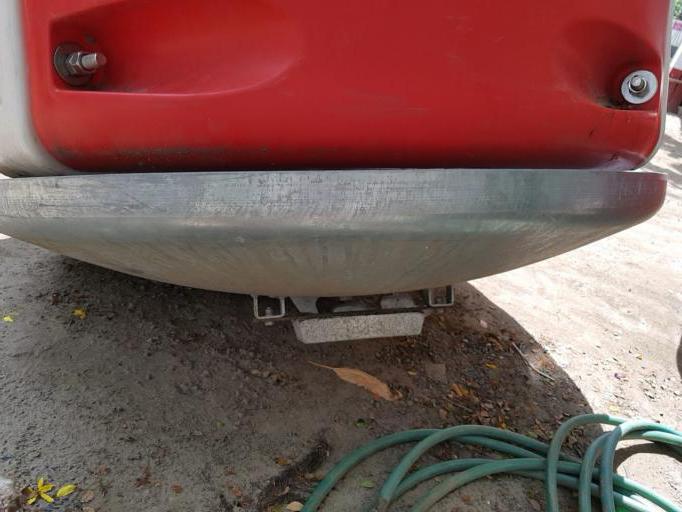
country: MM
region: Mandalay
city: Mandalay
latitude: 21.9725
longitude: 96.0581
